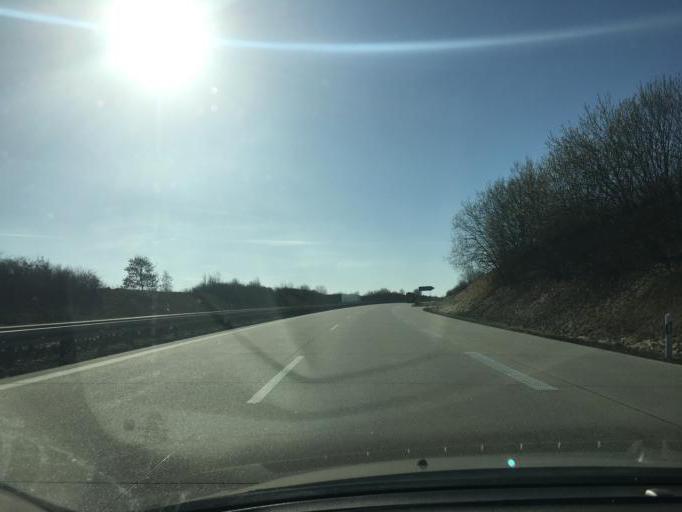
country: DE
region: Saxony
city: Muhlau
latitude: 50.8834
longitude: 12.7795
